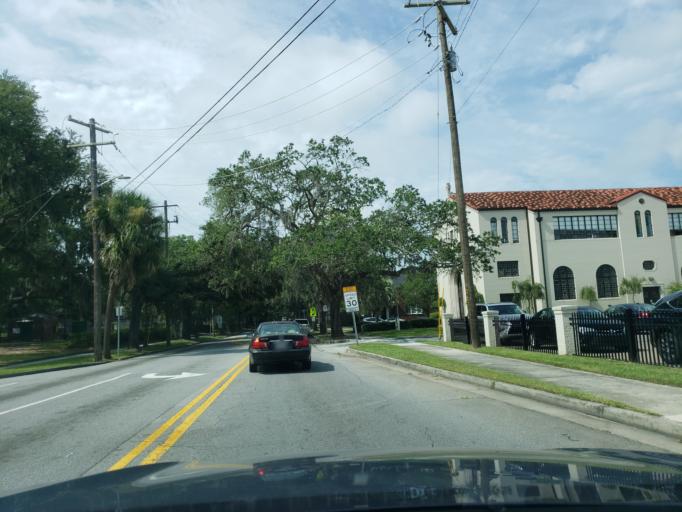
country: US
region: Georgia
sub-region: Chatham County
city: Savannah
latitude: 32.0481
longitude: -81.0854
